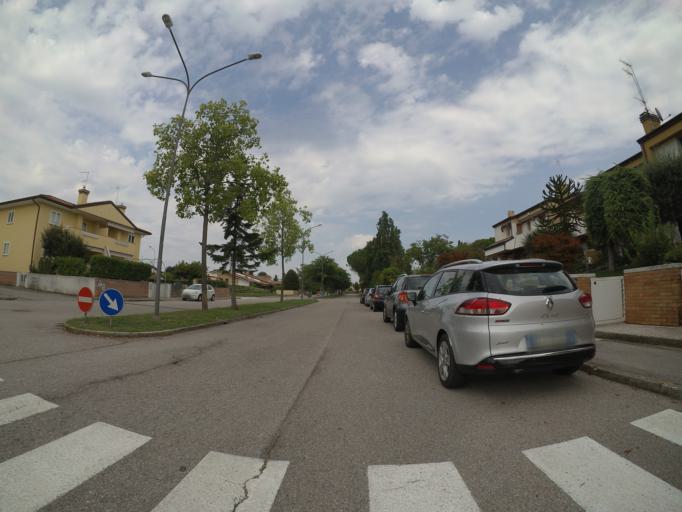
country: IT
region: Friuli Venezia Giulia
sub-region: Provincia di Udine
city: Codroipo
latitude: 45.9541
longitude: 12.9930
